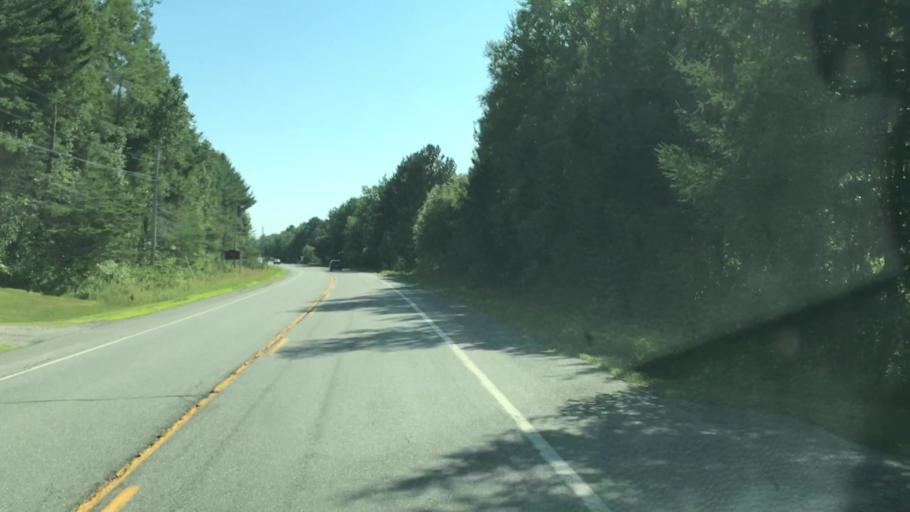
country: US
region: Maine
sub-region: Penobscot County
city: Enfield
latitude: 45.3259
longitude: -68.5939
